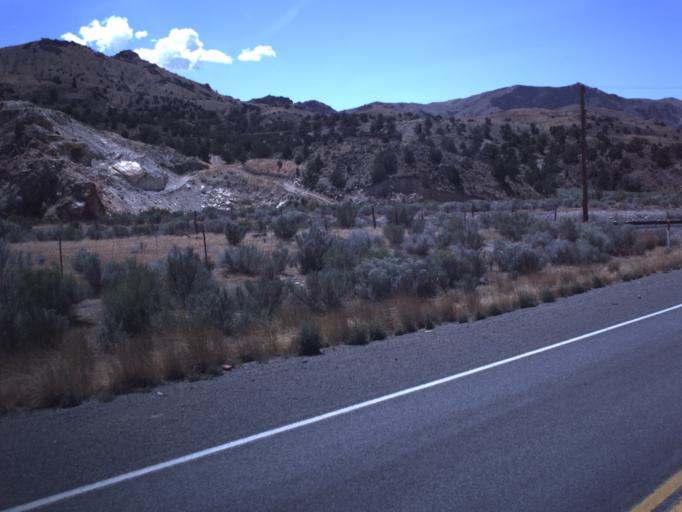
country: US
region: Utah
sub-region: Juab County
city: Nephi
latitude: 39.5879
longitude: -112.1655
